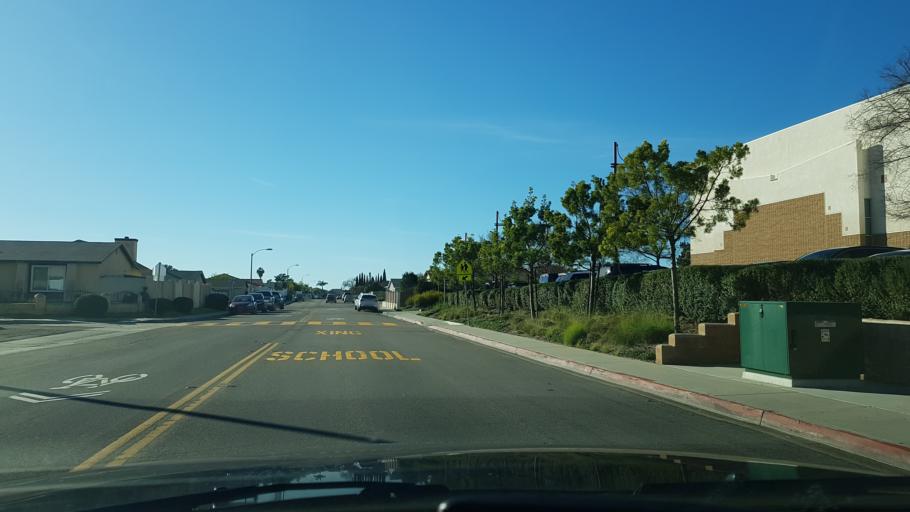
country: US
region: California
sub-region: San Diego County
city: Fairbanks Ranch
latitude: 32.9053
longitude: -117.1486
